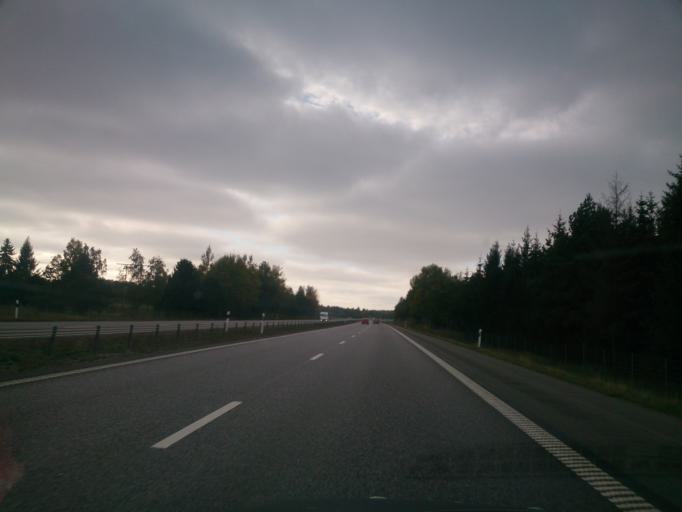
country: SE
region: OEstergoetland
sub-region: Linkopings Kommun
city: Linghem
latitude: 58.4648
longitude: 15.7998
